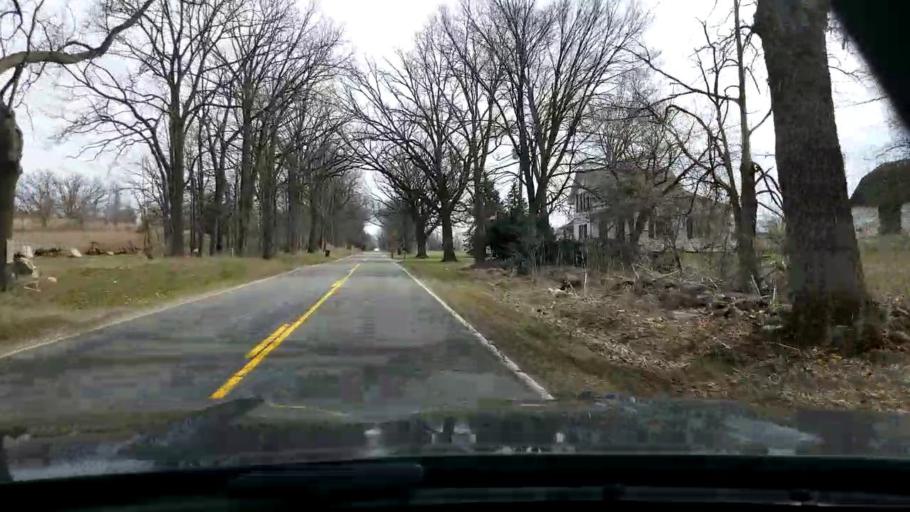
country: US
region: Michigan
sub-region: Jackson County
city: Spring Arbor
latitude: 42.1014
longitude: -84.5149
